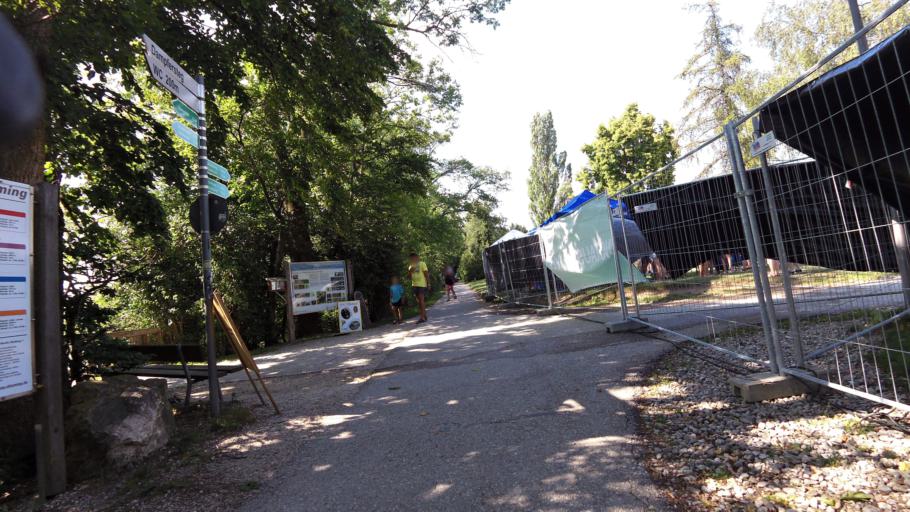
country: DE
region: Bavaria
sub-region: Upper Bavaria
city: Chieming
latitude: 47.8961
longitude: 12.5276
